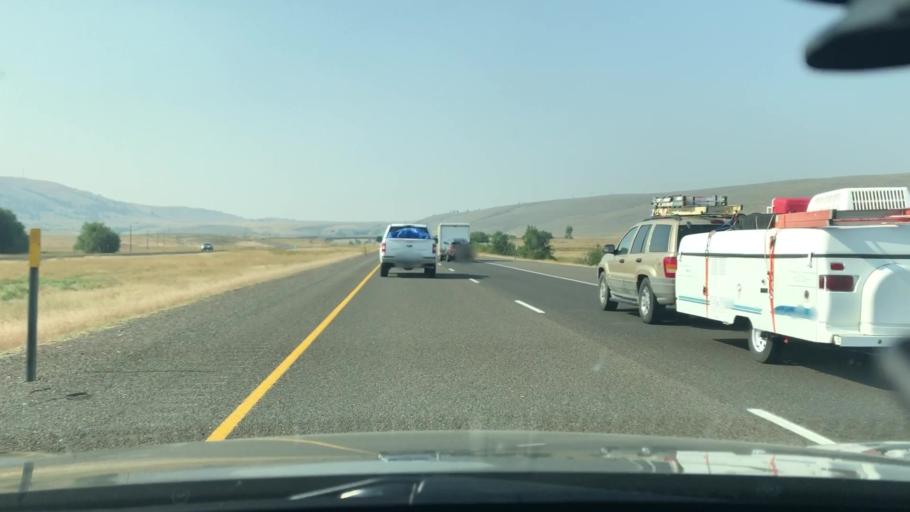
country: US
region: Oregon
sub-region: Union County
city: Union
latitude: 45.1175
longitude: -117.9602
